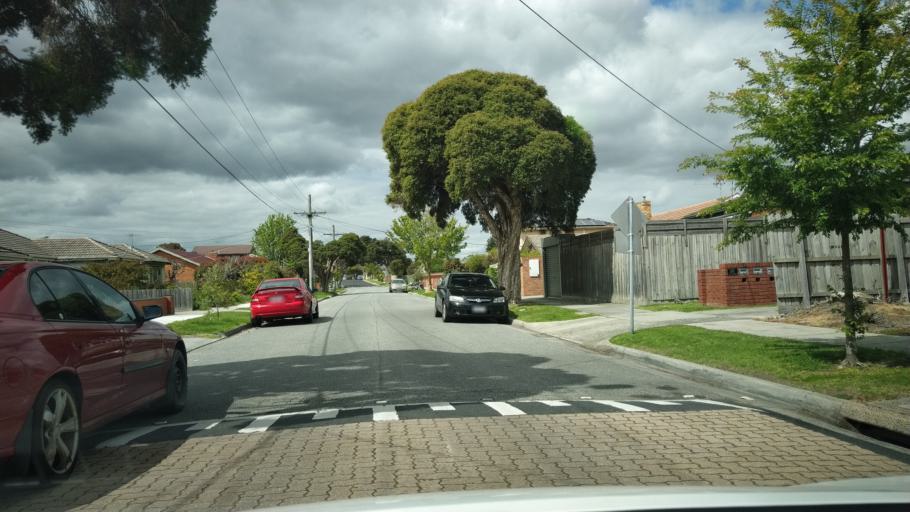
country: AU
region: Victoria
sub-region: Greater Dandenong
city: Noble Park
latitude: -37.9772
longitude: 145.1743
